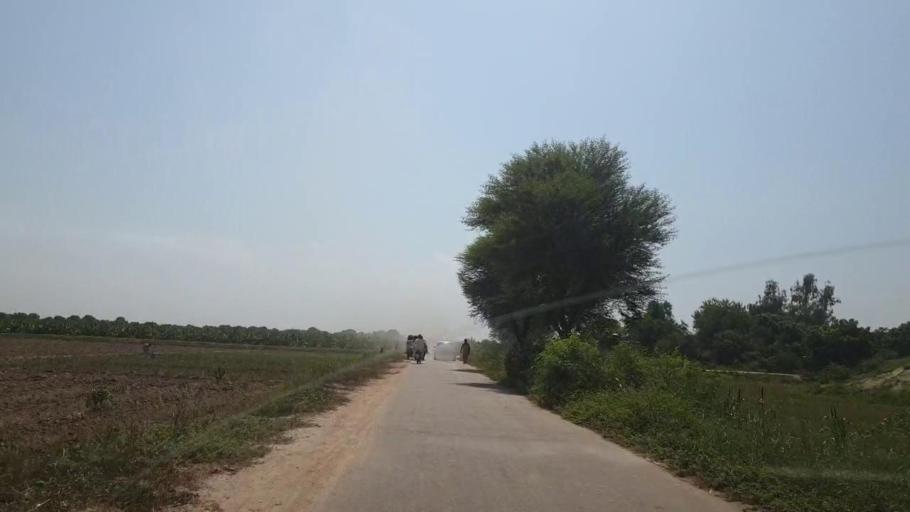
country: PK
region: Sindh
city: Tando Allahyar
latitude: 25.4002
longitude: 68.6439
